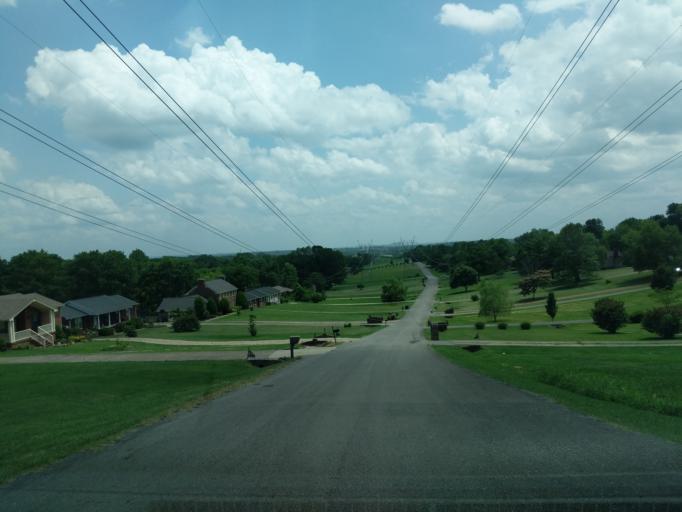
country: US
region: Tennessee
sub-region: Davidson County
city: Goodlettsville
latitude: 36.3103
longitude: -86.7283
